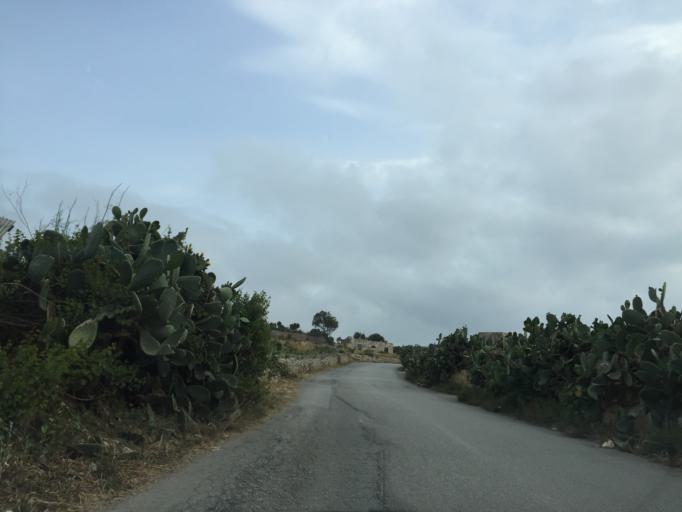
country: MT
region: L-Imgarr
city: Imgarr
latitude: 35.9329
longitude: 14.3512
